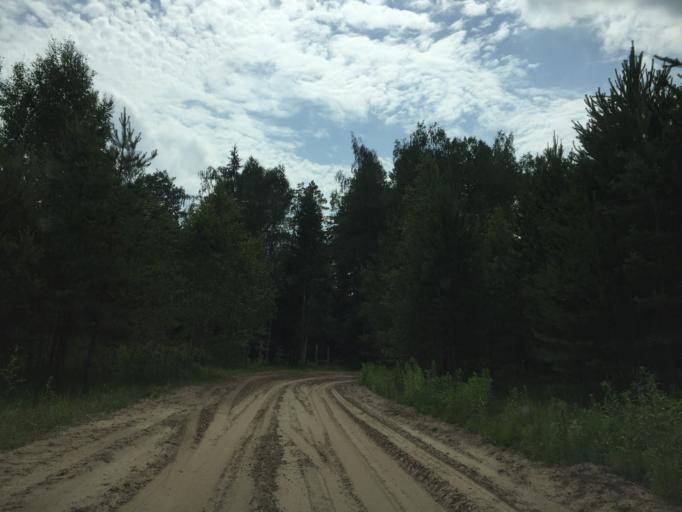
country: LV
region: Ozolnieku
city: Ozolnieki
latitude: 56.7559
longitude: 23.7514
